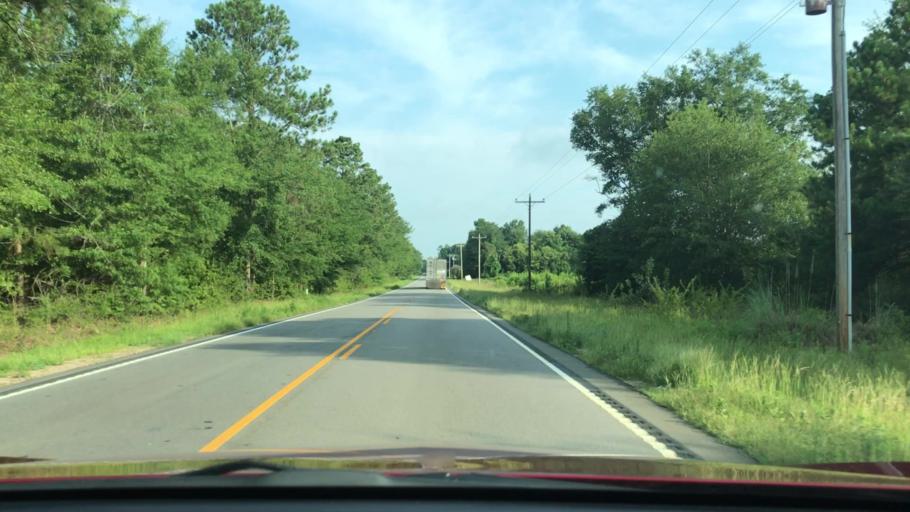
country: US
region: South Carolina
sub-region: Barnwell County
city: Blackville
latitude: 33.5532
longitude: -81.1610
